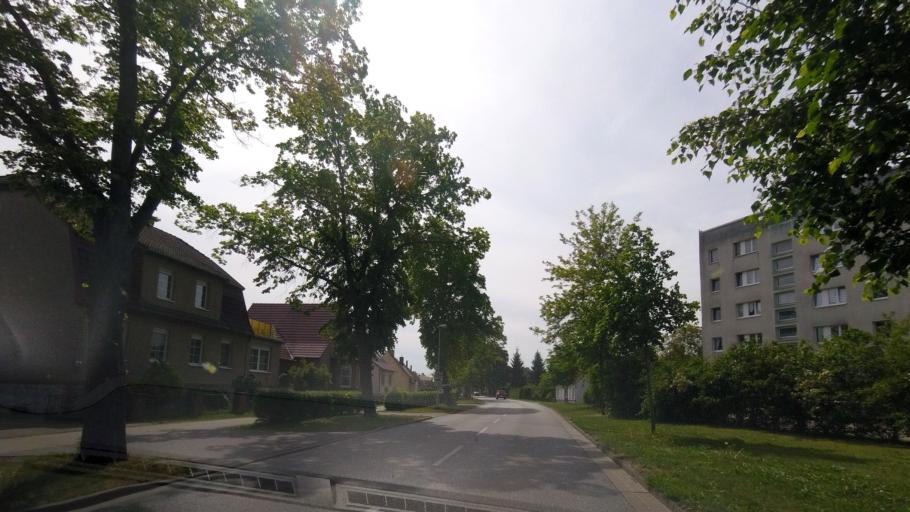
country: DE
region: Brandenburg
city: Wittstock
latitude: 53.1558
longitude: 12.4830
